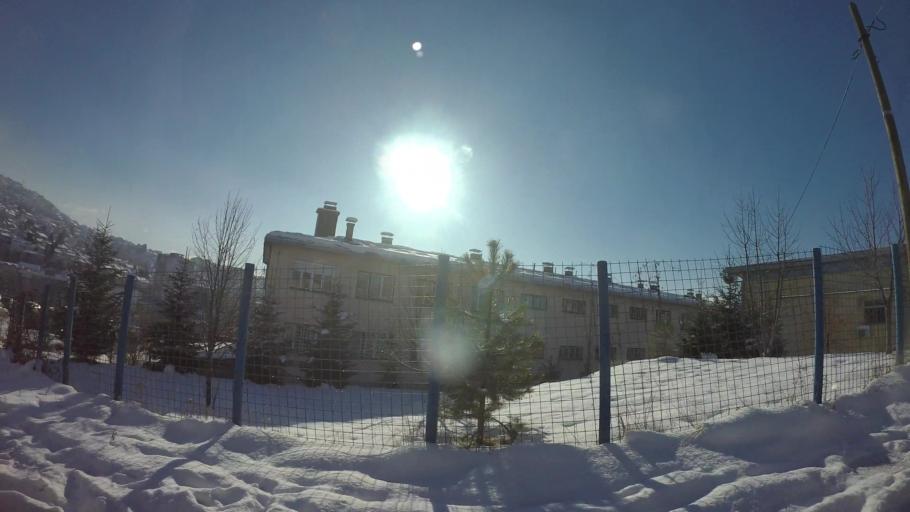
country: BA
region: Federation of Bosnia and Herzegovina
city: Kobilja Glava
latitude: 43.8766
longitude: 18.4089
